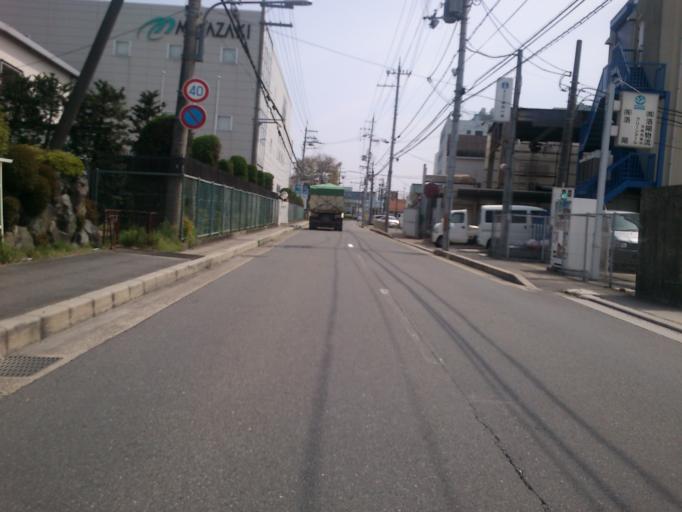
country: JP
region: Kyoto
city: Muko
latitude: 34.9272
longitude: 135.7151
